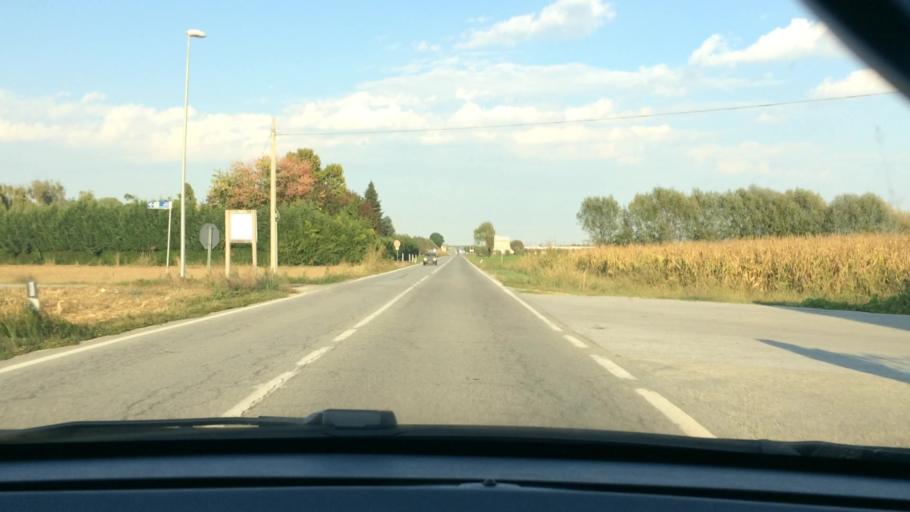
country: IT
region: Piedmont
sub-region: Provincia di Torino
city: Candiolo
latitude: 44.9510
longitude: 7.5730
